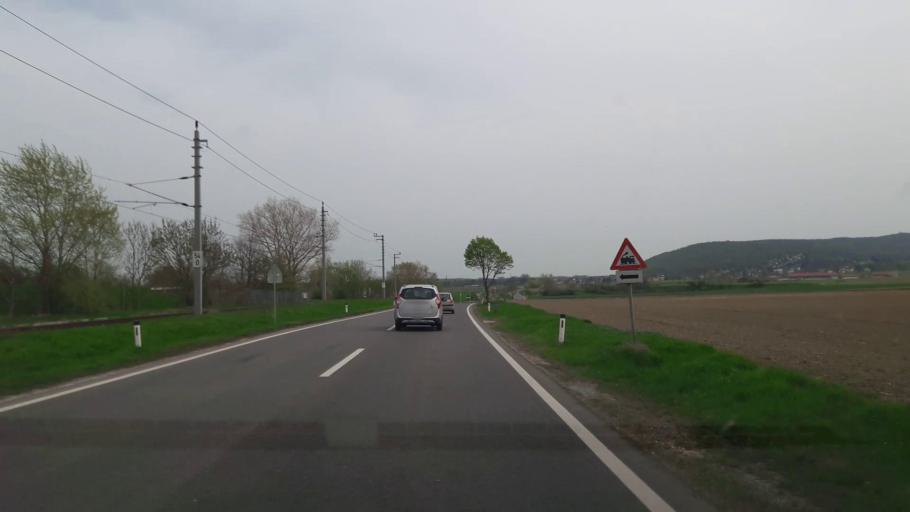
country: AT
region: Lower Austria
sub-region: Politischer Bezirk Bruck an der Leitha
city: Wolfsthal
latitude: 48.1434
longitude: 16.9792
